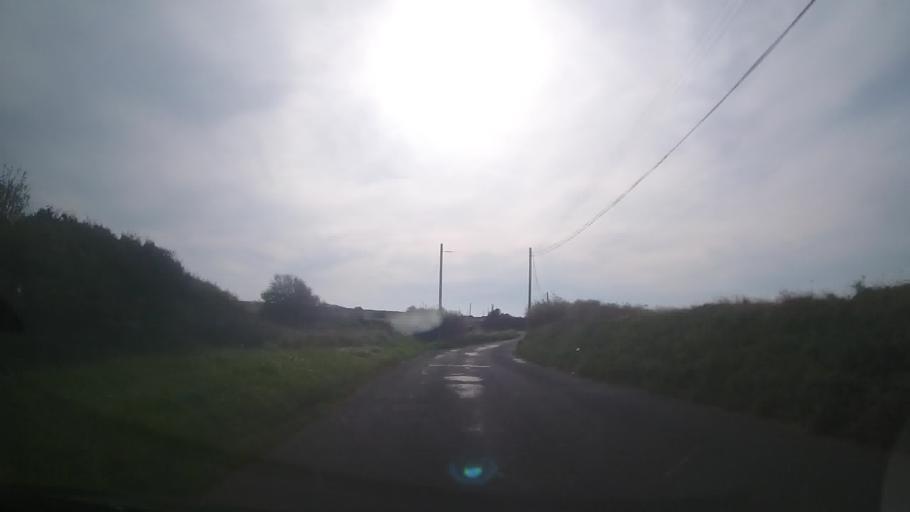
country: GB
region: Wales
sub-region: Pembrokeshire
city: Saint David's
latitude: 51.8911
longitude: -5.2530
